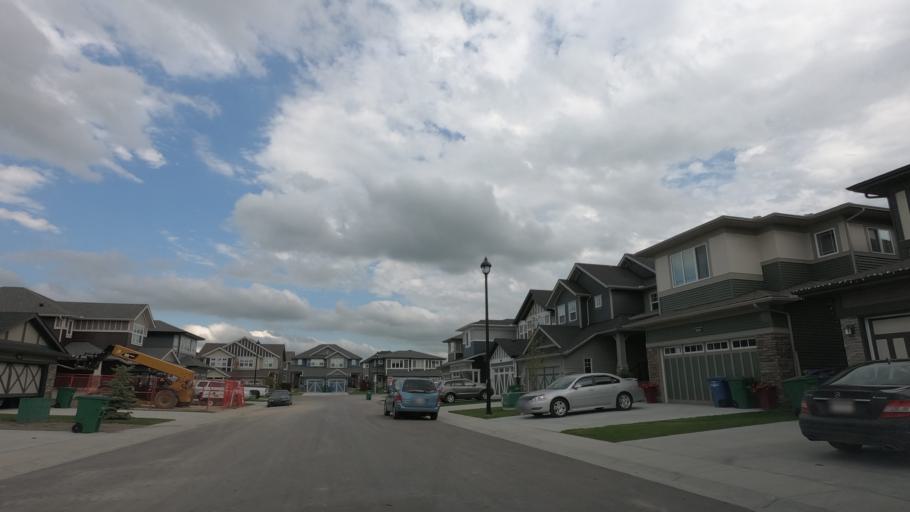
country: CA
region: Alberta
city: Airdrie
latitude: 51.2568
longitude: -113.9889
